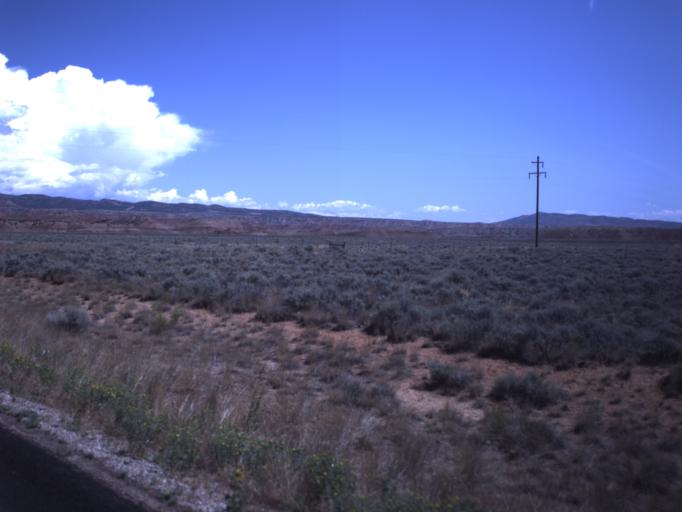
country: US
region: Utah
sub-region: Uintah County
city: Maeser
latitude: 40.4051
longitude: -109.7667
